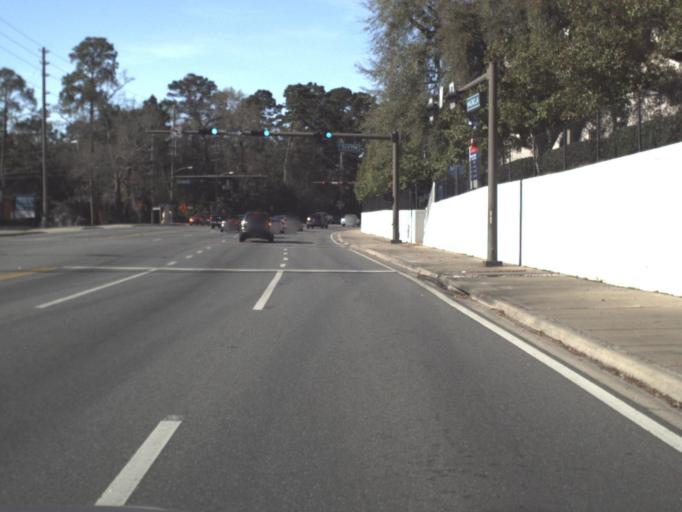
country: US
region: Florida
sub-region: Leon County
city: Tallahassee
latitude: 30.4560
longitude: -84.2625
